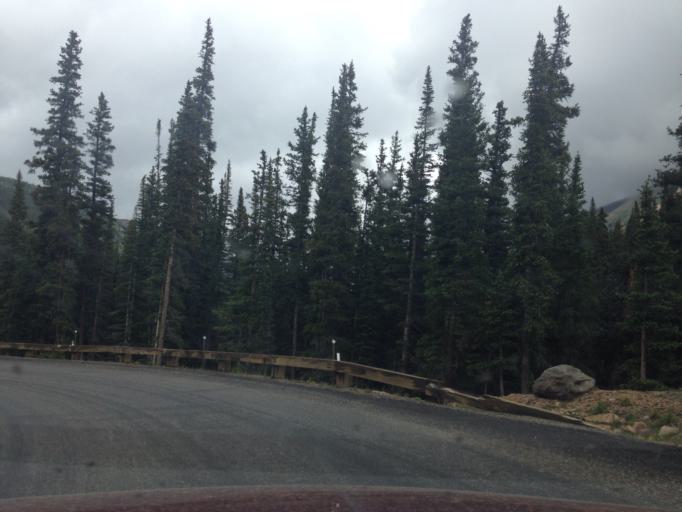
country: US
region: Colorado
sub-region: Clear Creek County
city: Georgetown
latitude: 39.6092
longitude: -105.7148
